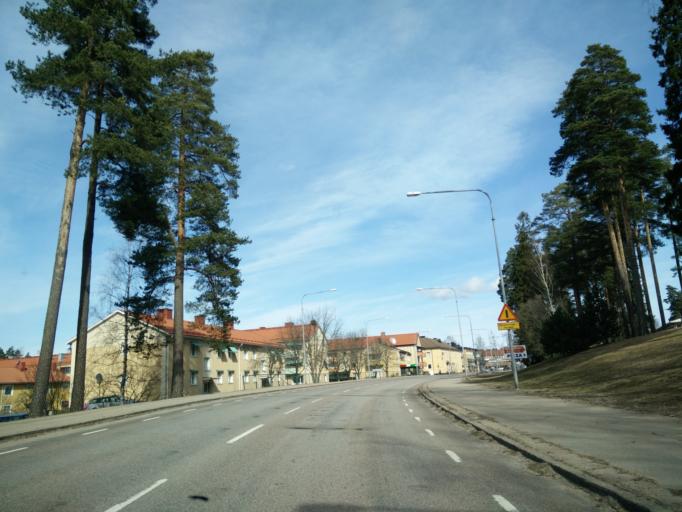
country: SE
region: Vaermland
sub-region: Hagfors Kommun
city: Hagfors
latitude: 60.0292
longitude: 13.6994
